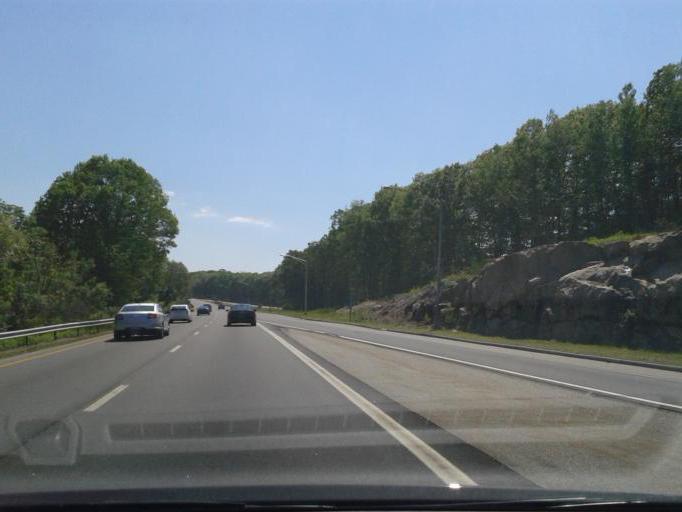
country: US
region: Connecticut
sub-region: New London County
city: Pawcatuck
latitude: 41.4145
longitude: -71.8532
